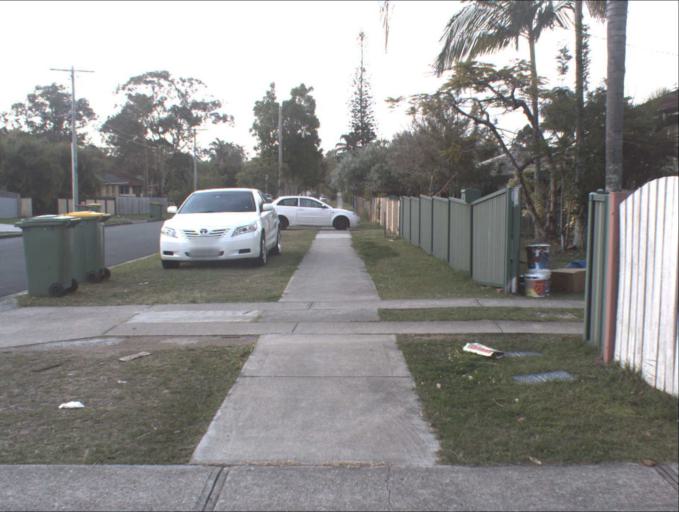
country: AU
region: Queensland
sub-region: Logan
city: Waterford West
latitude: -27.6776
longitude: 153.1290
